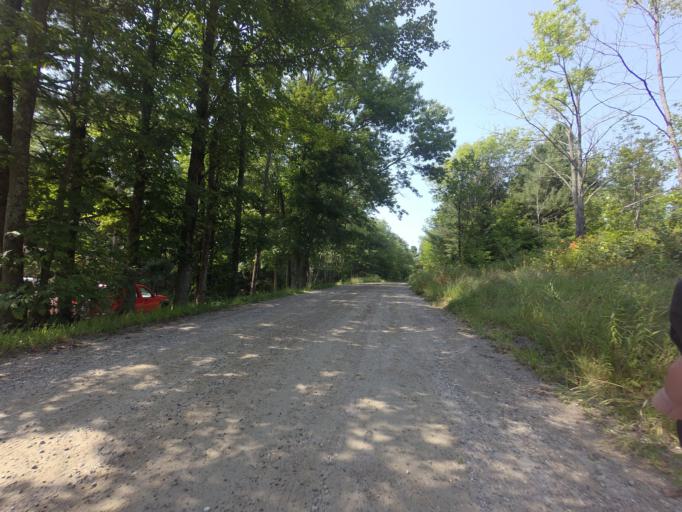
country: CA
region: Ontario
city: Skatepark
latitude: 44.6969
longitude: -76.7566
